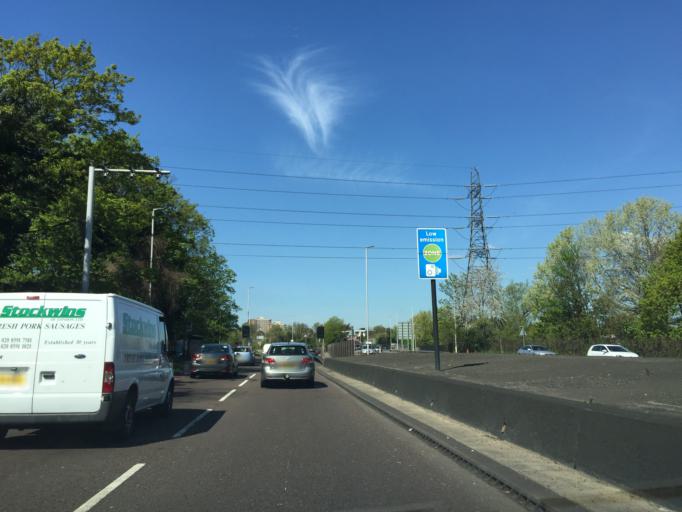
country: GB
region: England
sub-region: Greater London
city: Ilford
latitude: 51.5759
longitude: 0.0422
